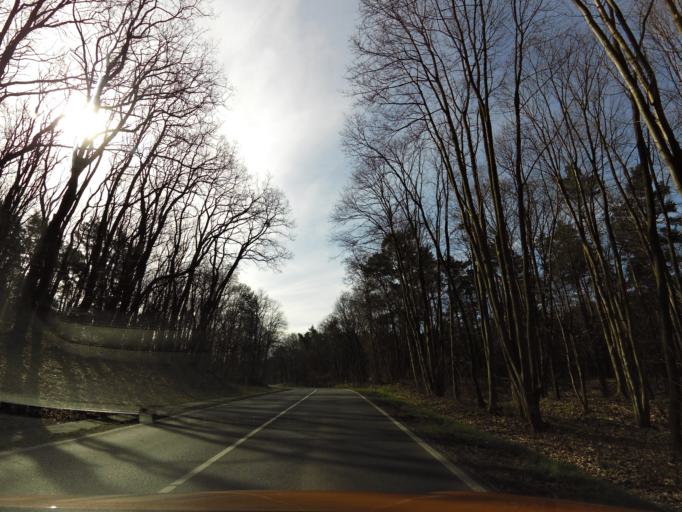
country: DE
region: Brandenburg
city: Michendorf
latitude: 52.3526
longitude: 13.0439
